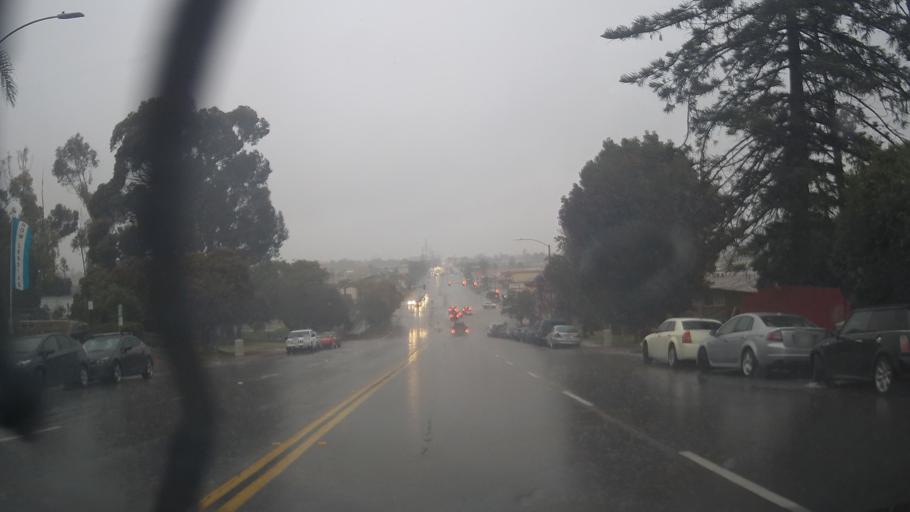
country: US
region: California
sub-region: San Diego County
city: Chula Vista
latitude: 32.6480
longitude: -117.0871
